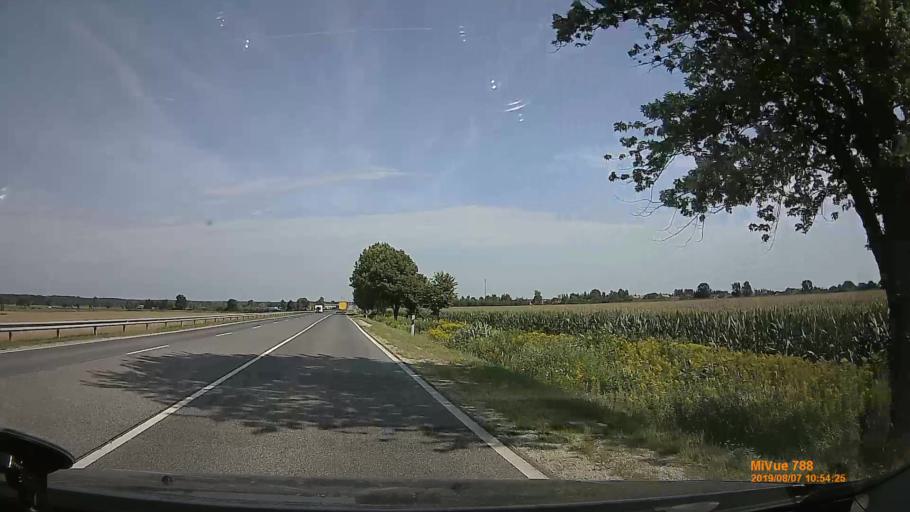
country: SI
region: Lendava-Lendva
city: Lendava
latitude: 46.6094
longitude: 16.4637
